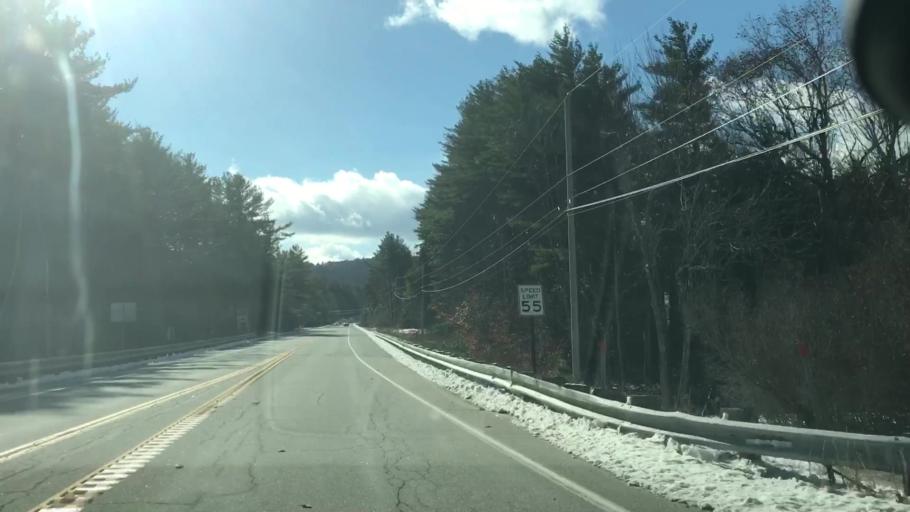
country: US
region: New Hampshire
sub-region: Carroll County
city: Ossipee
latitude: 43.6850
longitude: -71.1218
